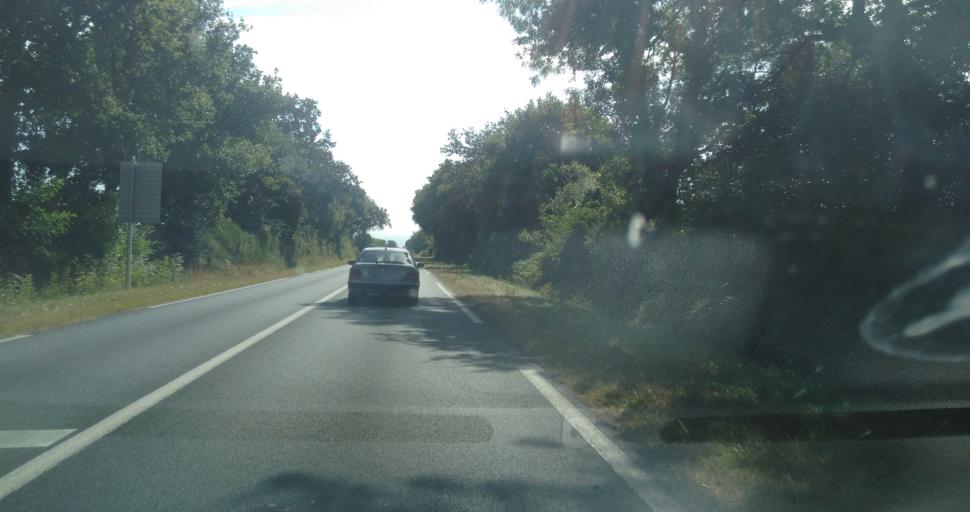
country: FR
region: Pays de la Loire
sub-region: Departement de la Vendee
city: Sainte-Foy
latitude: 46.4778
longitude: -1.6771
